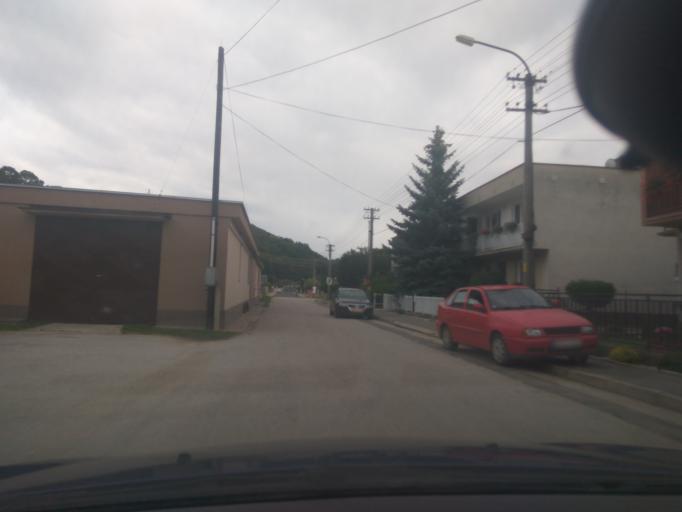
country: SK
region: Trenciansky
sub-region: Okres Nove Mesto nad Vahom
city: Nove Mesto nad Vahom
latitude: 48.6955
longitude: 17.8821
